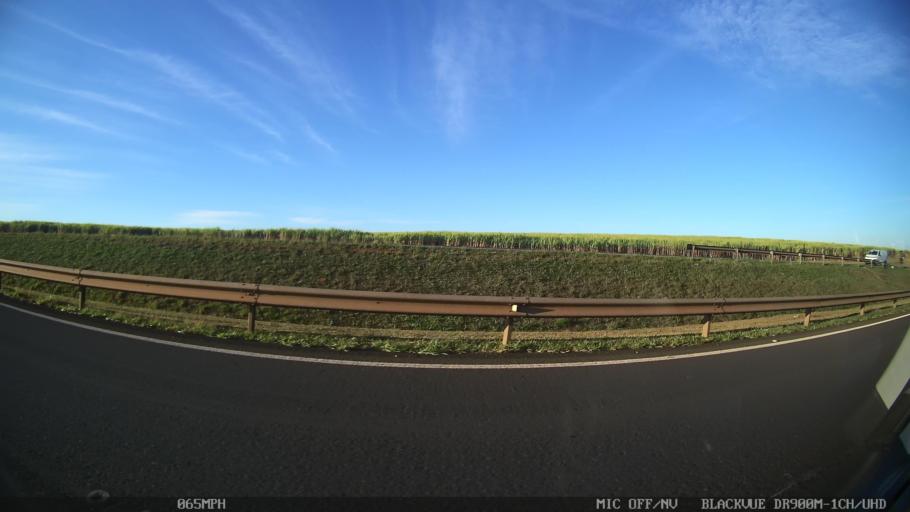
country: BR
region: Sao Paulo
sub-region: Urupes
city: Urupes
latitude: -21.0235
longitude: -49.1633
